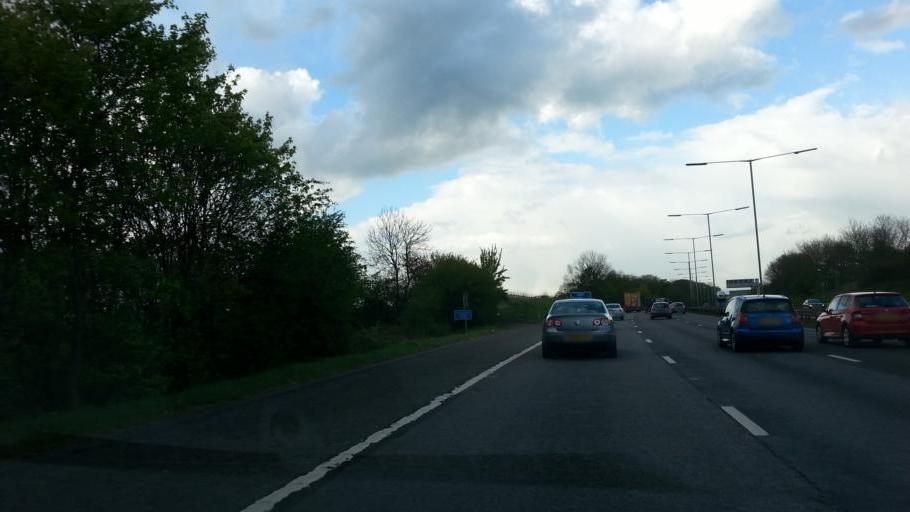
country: GB
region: England
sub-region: Warwickshire
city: Bedworth
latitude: 52.4491
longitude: -1.4243
